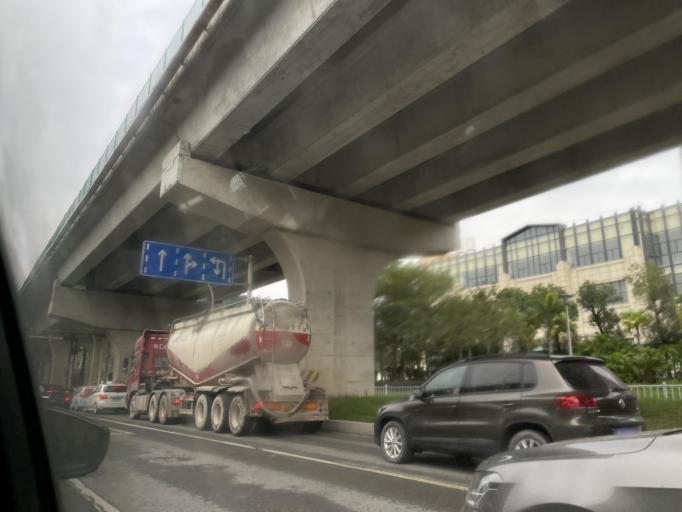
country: CN
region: Guangdong
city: Nanping
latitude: 22.1765
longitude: 113.4749
